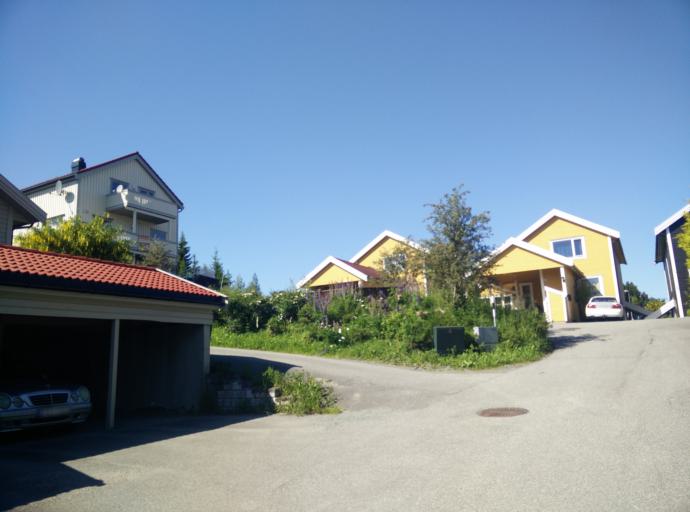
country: NO
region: Sor-Trondelag
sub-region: Trondheim
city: Trondheim
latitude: 63.4126
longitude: 10.3715
